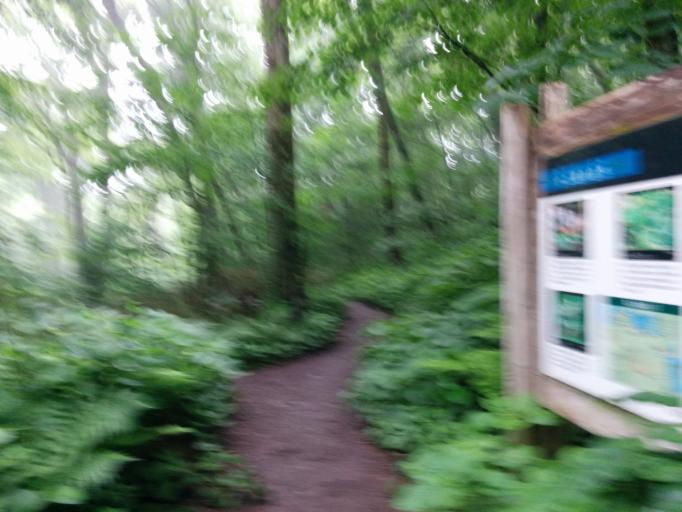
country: JP
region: Akita
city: Noshiromachi
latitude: 40.5628
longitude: 139.9796
